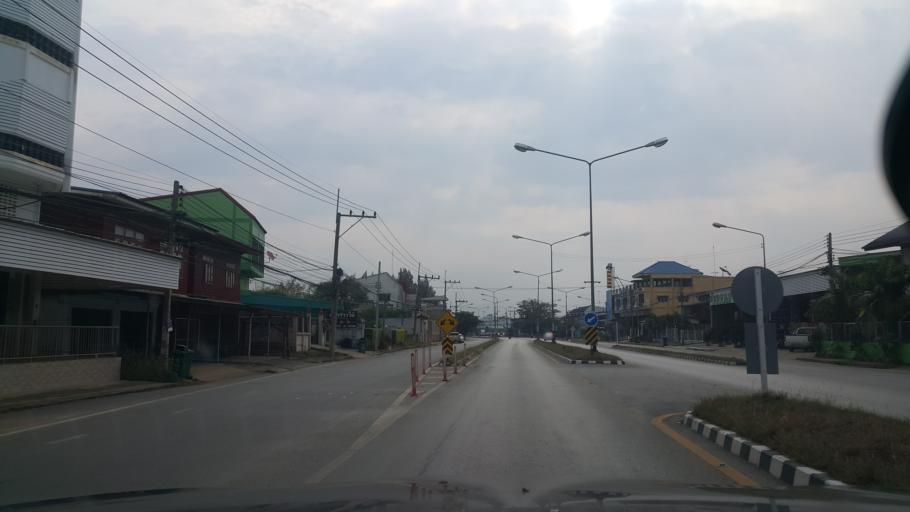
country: TH
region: Sukhothai
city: Si Samrong
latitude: 17.1712
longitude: 99.8578
